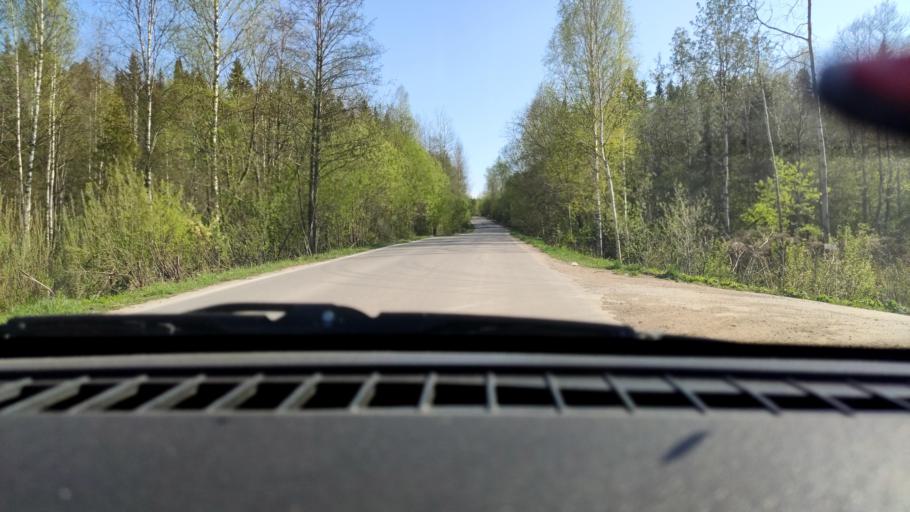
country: RU
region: Perm
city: Overyata
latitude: 58.0764
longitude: 56.0019
